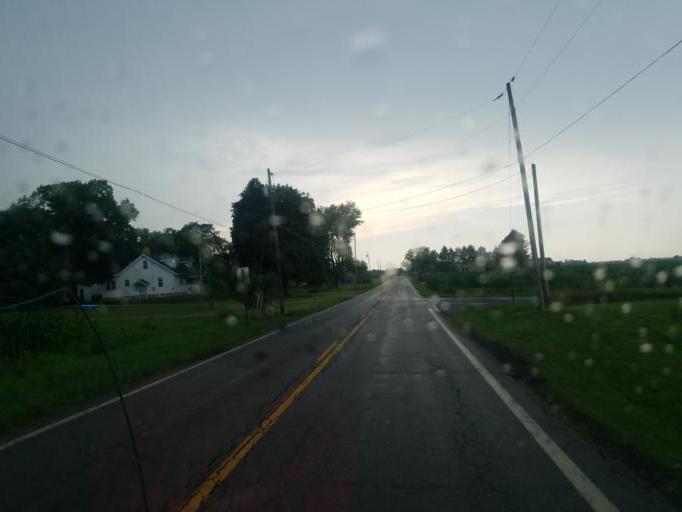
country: US
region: Ohio
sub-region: Wayne County
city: Rittman
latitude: 40.9457
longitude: -81.8210
